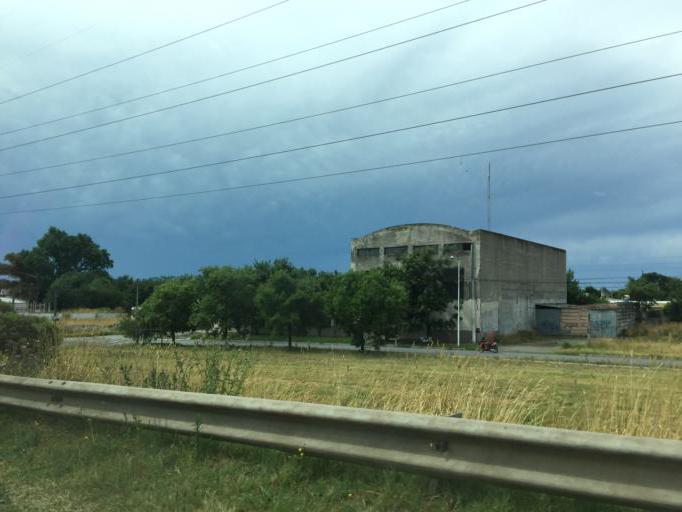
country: AR
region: Buenos Aires
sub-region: Partido de Tandil
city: Tandil
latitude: -37.3023
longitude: -59.1260
